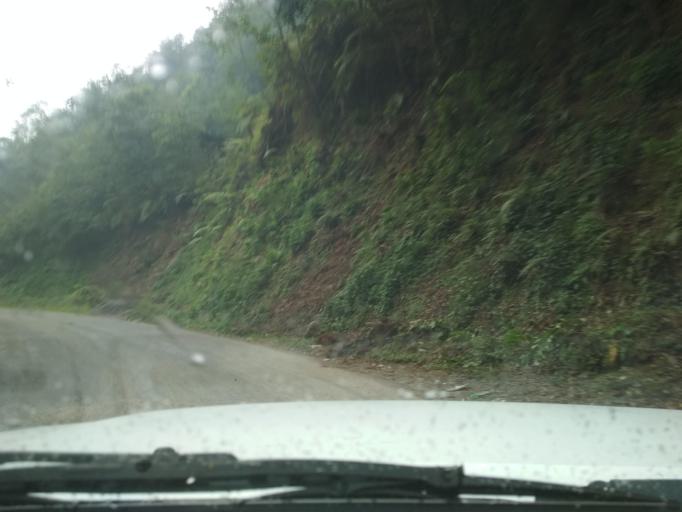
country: MX
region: Veracruz
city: La Perla
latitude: 18.9376
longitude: -97.1494
